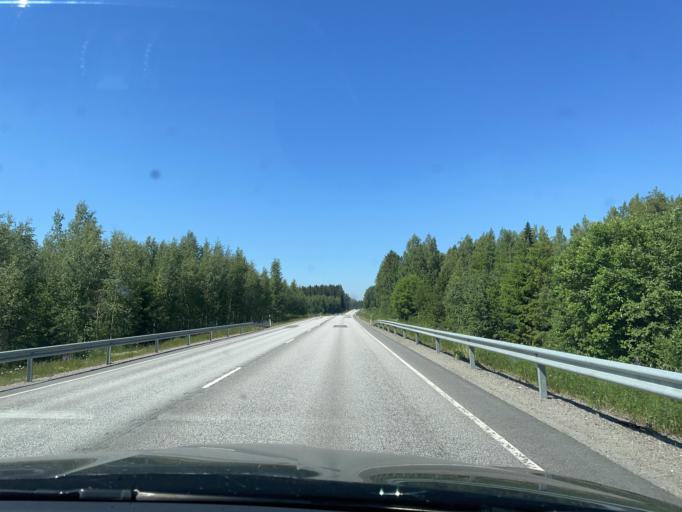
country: FI
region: Central Finland
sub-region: Saarijaervi-Viitasaari
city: Viitasaari
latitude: 63.1430
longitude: 25.8246
